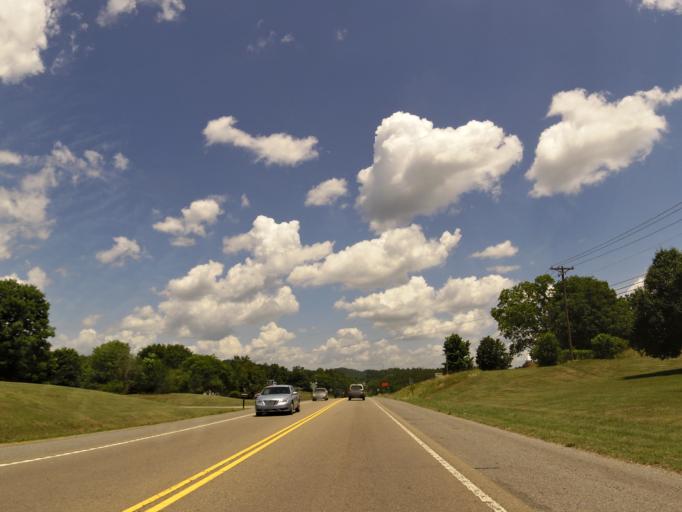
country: US
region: Tennessee
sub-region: Union County
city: Condon
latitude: 36.1713
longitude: -83.9049
